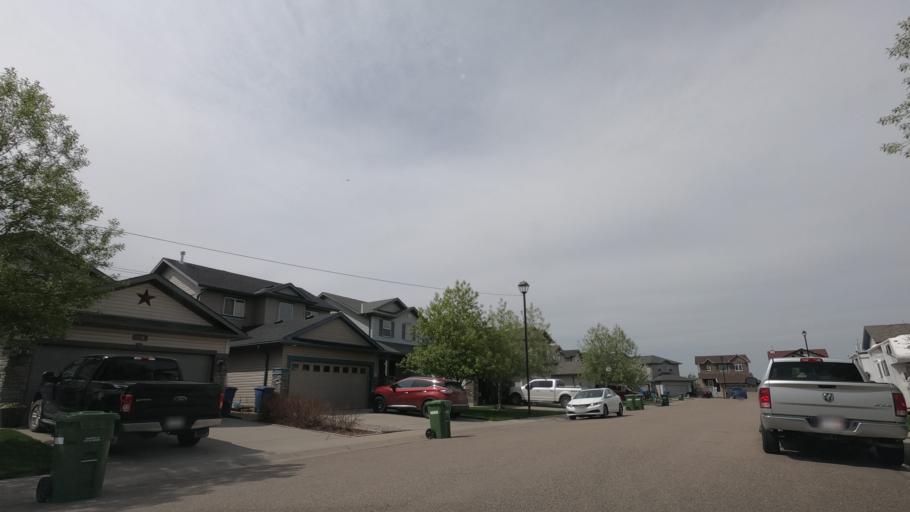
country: CA
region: Alberta
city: Airdrie
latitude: 51.3062
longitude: -114.0243
